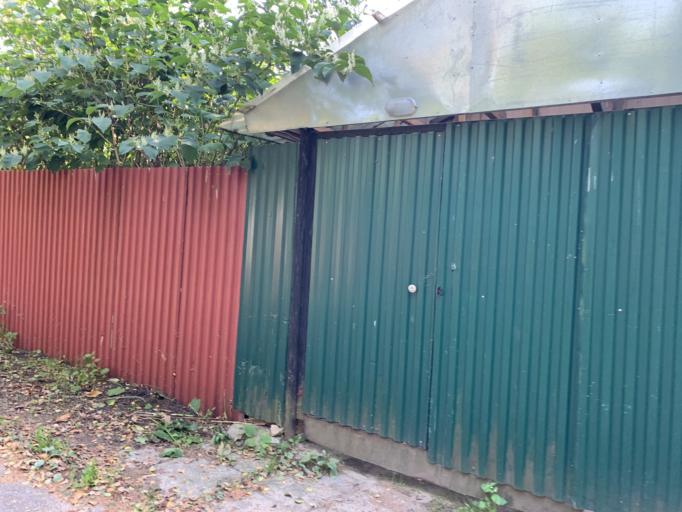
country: RU
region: Moskovskaya
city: Mamontovka
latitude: 55.9655
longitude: 37.8281
